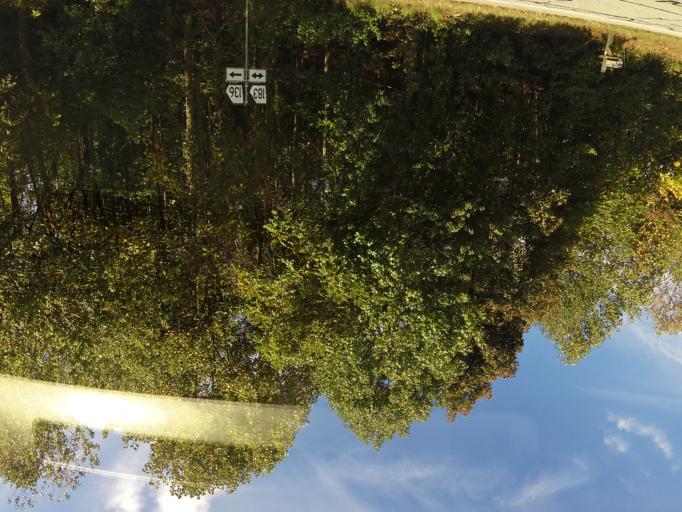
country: US
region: Georgia
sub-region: Dawson County
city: Dawsonville
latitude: 34.5260
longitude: -84.2523
